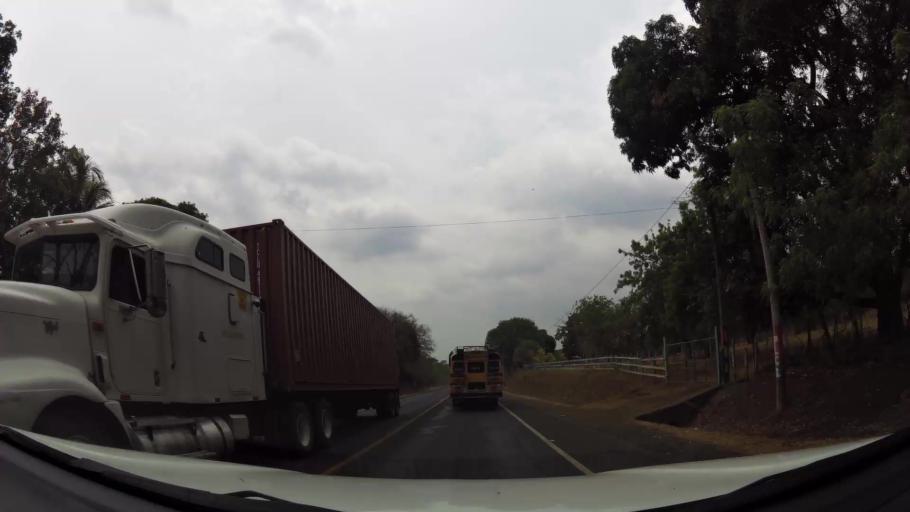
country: NI
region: Leon
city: Telica
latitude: 12.5147
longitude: -86.8628
